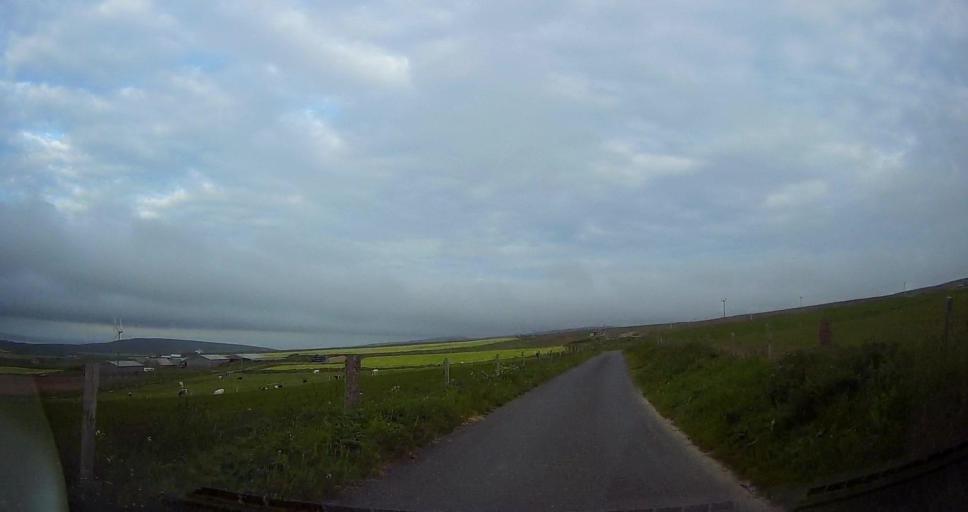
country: GB
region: Scotland
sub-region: Orkney Islands
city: Orkney
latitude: 59.1197
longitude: -3.1333
